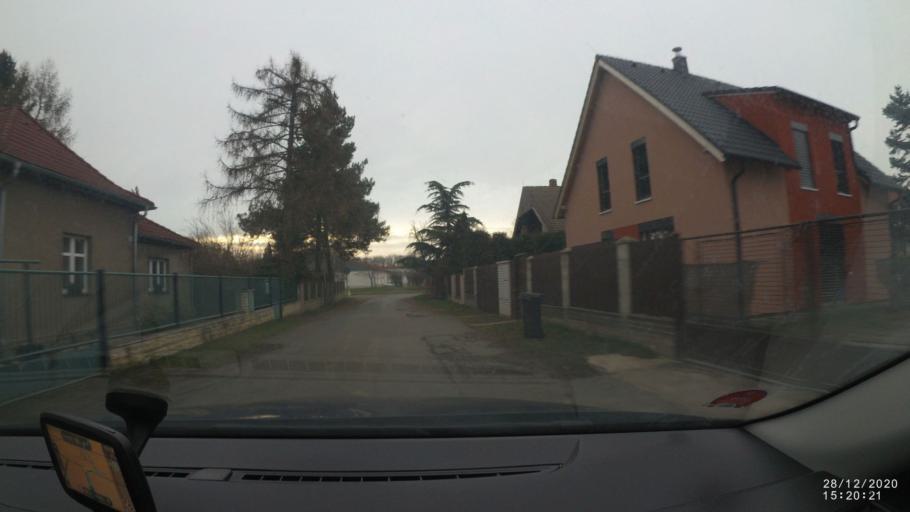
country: CZ
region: Central Bohemia
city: Sestajovice
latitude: 50.0744
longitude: 14.6597
